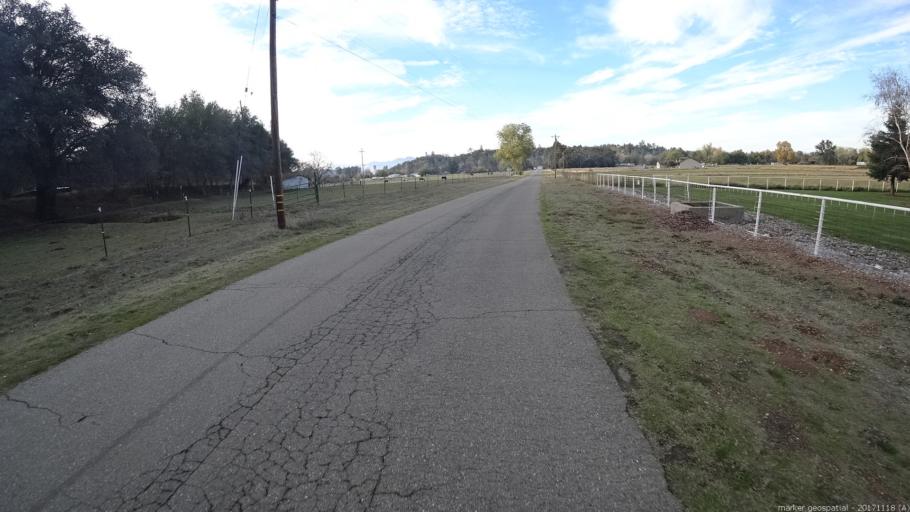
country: US
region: California
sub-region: Shasta County
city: Anderson
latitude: 40.4557
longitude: -122.3312
